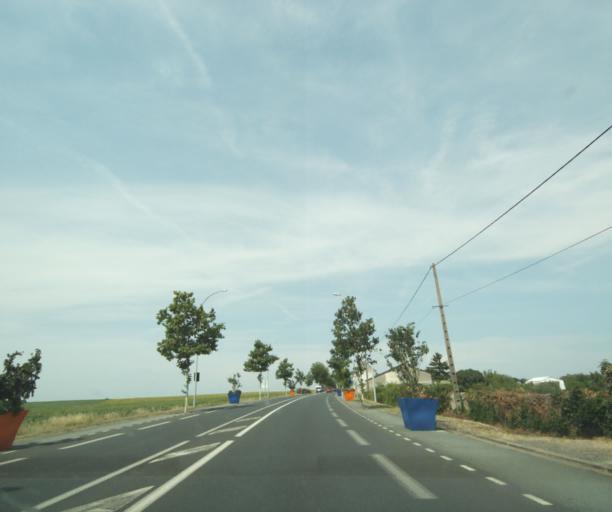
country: FR
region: Centre
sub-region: Departement d'Indre-et-Loire
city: Sainte-Maure-de-Touraine
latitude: 47.1181
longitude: 0.6206
